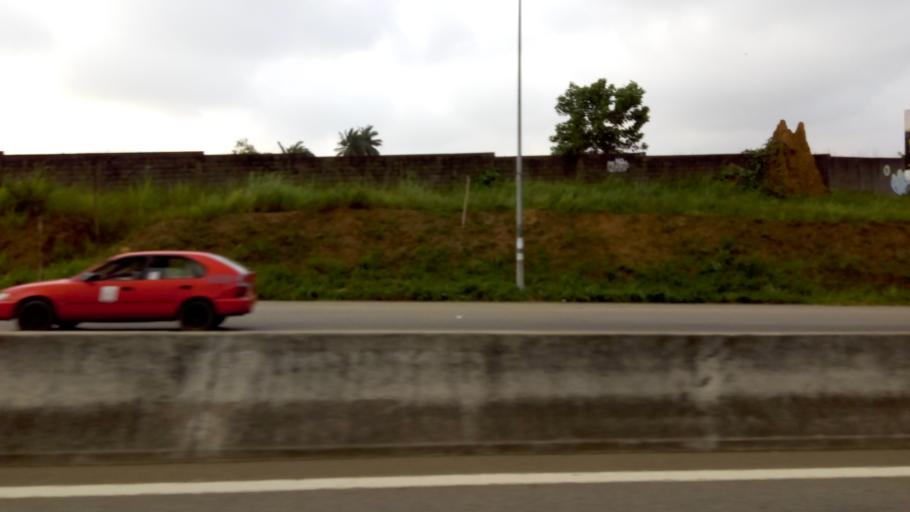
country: CI
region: Lagunes
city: Abidjan
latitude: 5.3513
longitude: -3.9845
